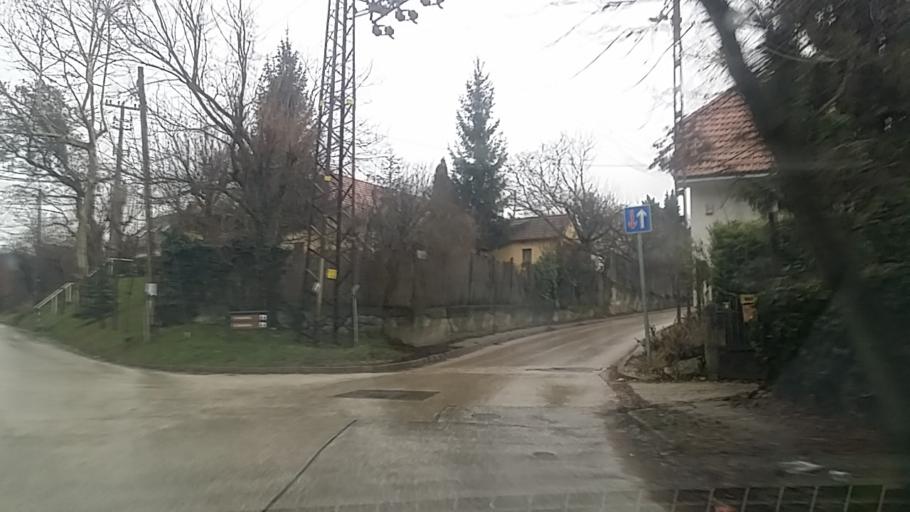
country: HU
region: Pest
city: Budakeszi
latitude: 47.5086
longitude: 18.9283
